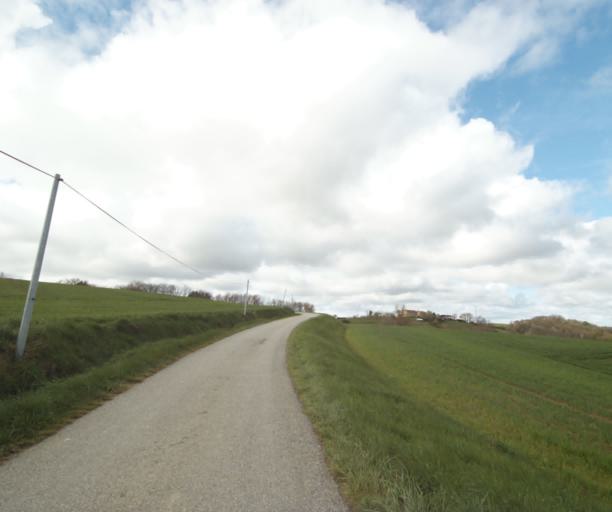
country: FR
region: Midi-Pyrenees
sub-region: Departement de l'Ariege
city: Saverdun
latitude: 43.1990
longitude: 1.5395
